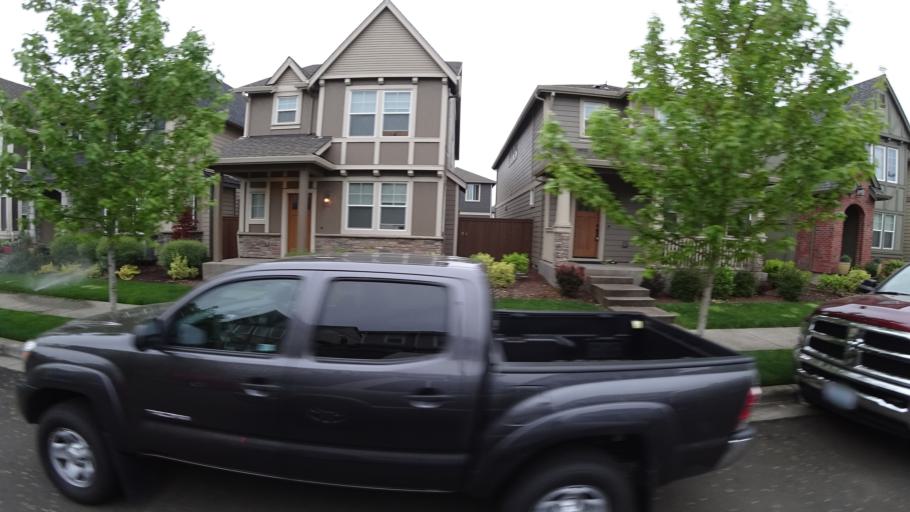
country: US
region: Oregon
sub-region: Washington County
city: Aloha
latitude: 45.5167
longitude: -122.8827
